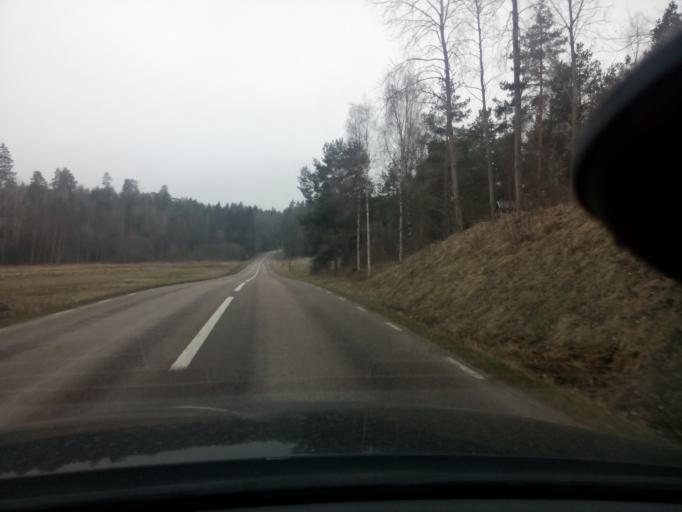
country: SE
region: Soedermanland
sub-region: Gnesta Kommun
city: Gnesta
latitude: 58.9946
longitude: 17.1684
